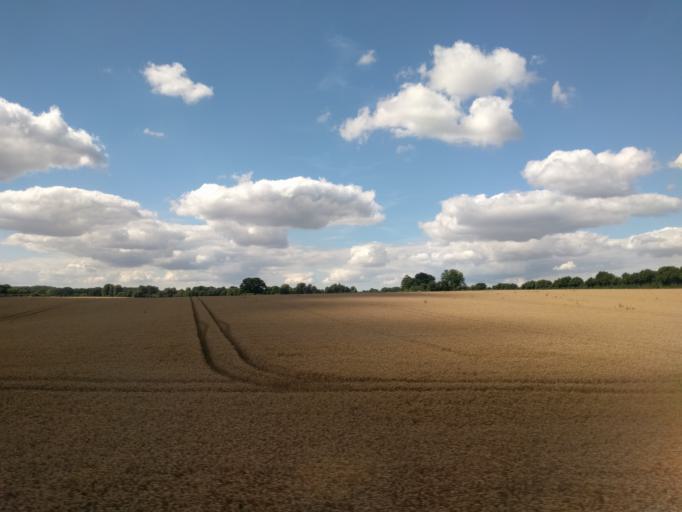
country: DK
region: Zealand
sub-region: Koge Kommune
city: Borup
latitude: 55.4907
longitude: 11.9710
